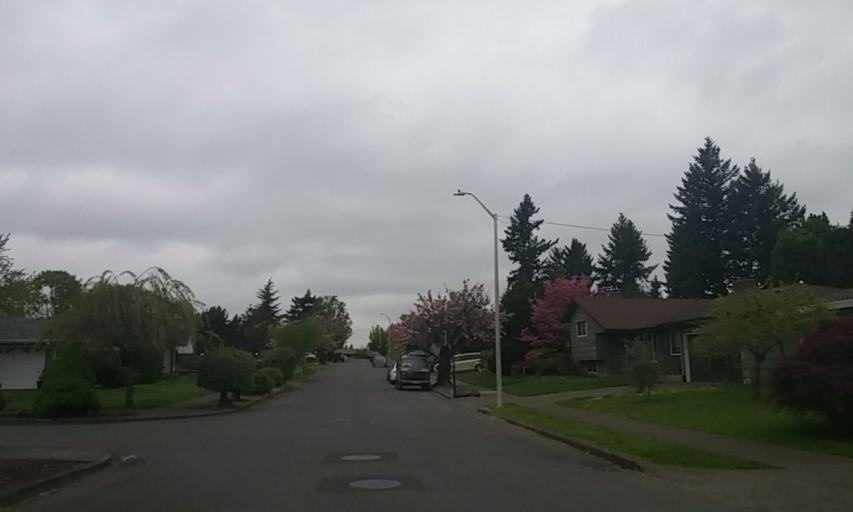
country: US
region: Oregon
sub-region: Multnomah County
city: Lents
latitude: 45.5073
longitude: -122.5584
